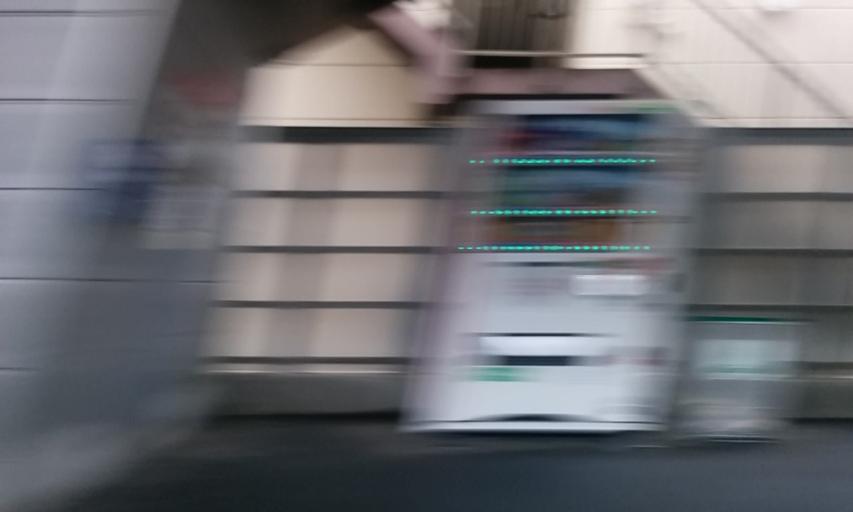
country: JP
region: Tokyo
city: Hino
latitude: 35.6574
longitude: 139.4311
